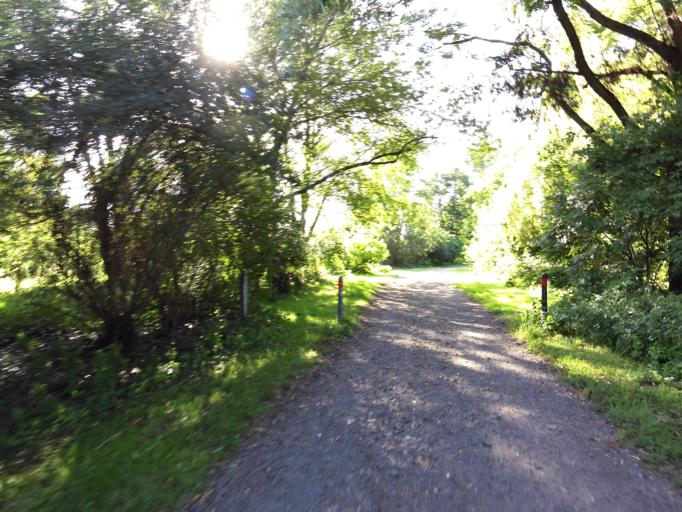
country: DE
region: Saxony
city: Markkleeberg
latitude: 51.2943
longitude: 12.4003
